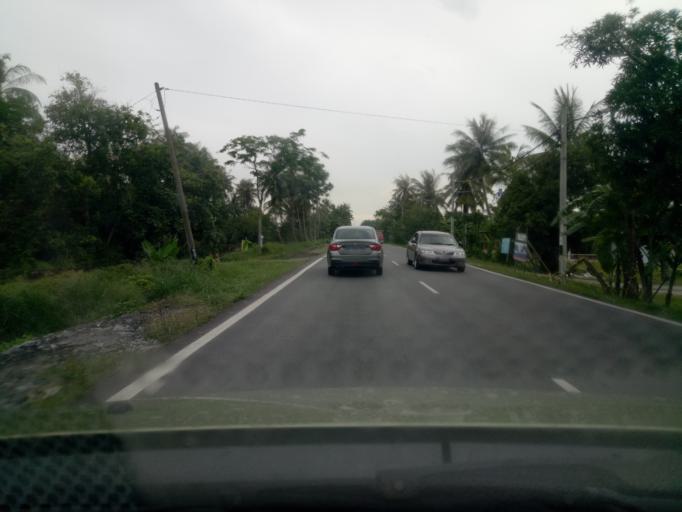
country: MY
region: Kedah
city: Alor Setar
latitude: 5.9724
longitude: 100.4119
